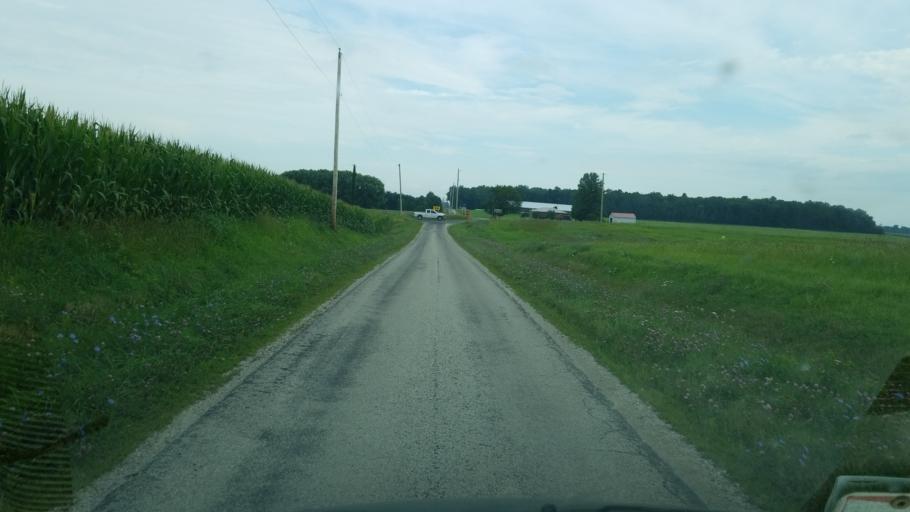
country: US
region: Ohio
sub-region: Seneca County
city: Tiffin
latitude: 40.9925
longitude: -83.0552
